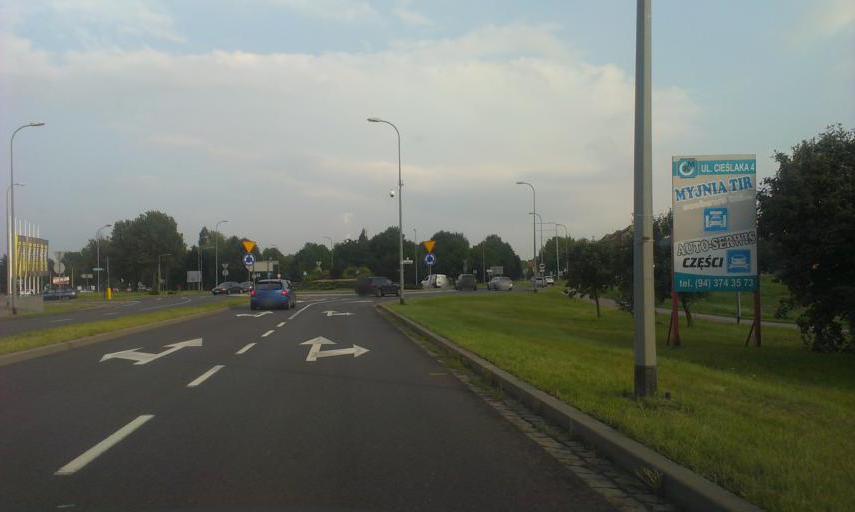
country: PL
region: West Pomeranian Voivodeship
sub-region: Powiat szczecinecki
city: Szczecinek
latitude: 53.7217
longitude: 16.6798
